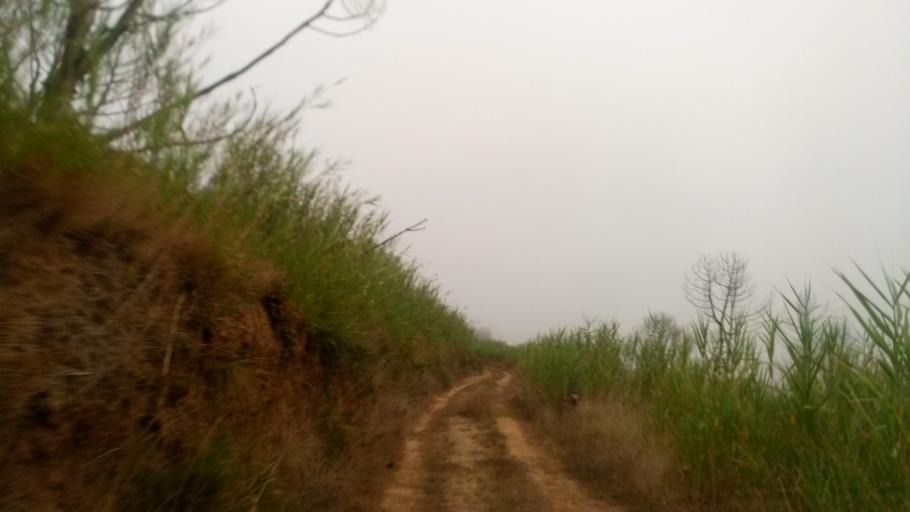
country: PT
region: Leiria
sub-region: Caldas da Rainha
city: Caldas da Rainha
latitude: 39.4665
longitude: -9.1966
